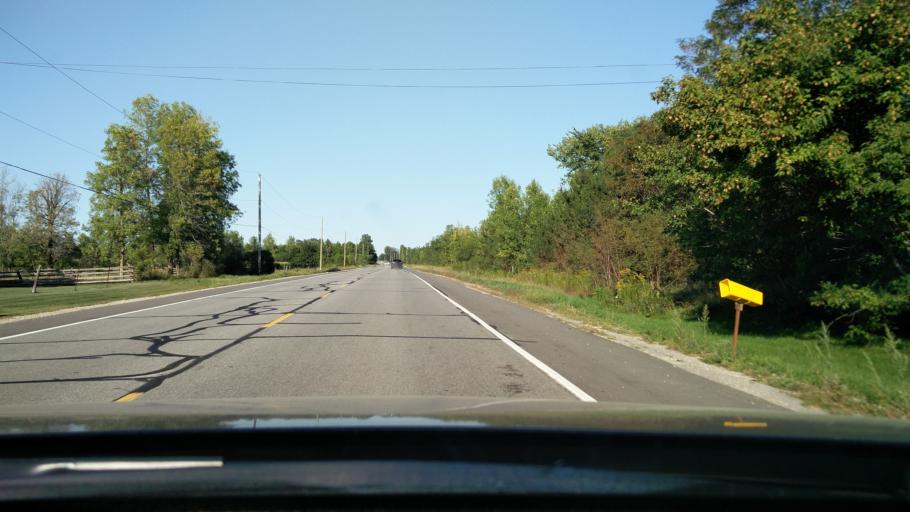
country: CA
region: Ontario
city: Perth
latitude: 44.9573
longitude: -76.1584
